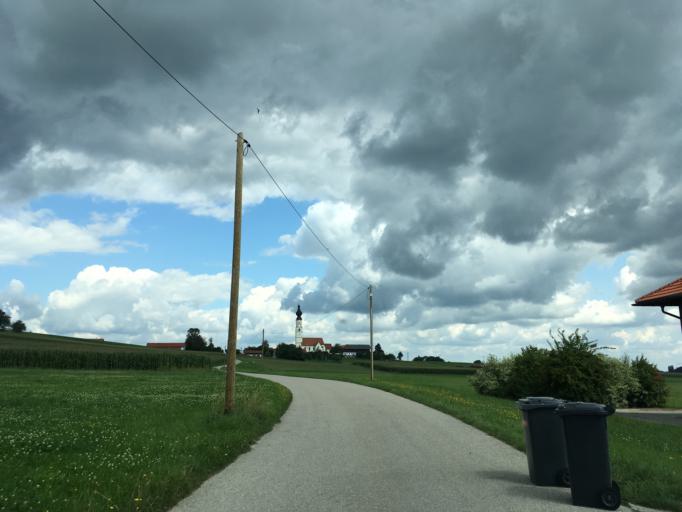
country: DE
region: Bavaria
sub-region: Upper Bavaria
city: Pittenhart
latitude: 48.0122
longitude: 12.3660
